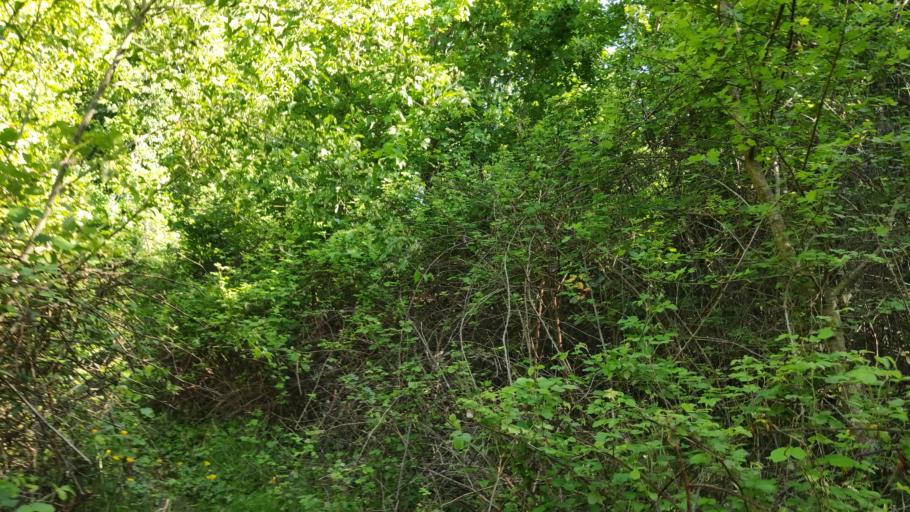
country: IT
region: Umbria
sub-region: Provincia di Terni
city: Fornole
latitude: 42.5486
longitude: 12.4399
